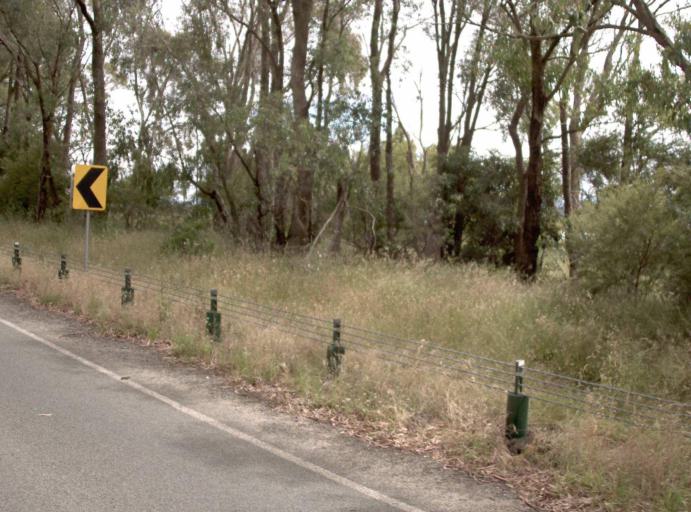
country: AU
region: Victoria
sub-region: Latrobe
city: Moe
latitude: -38.0980
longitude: 146.2340
